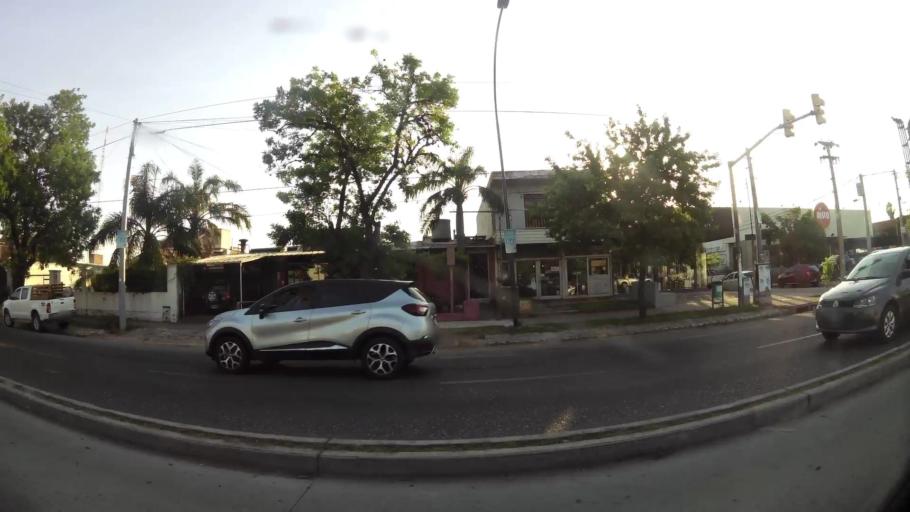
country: AR
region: Cordoba
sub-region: Departamento de Capital
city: Cordoba
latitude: -31.3770
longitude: -64.2256
